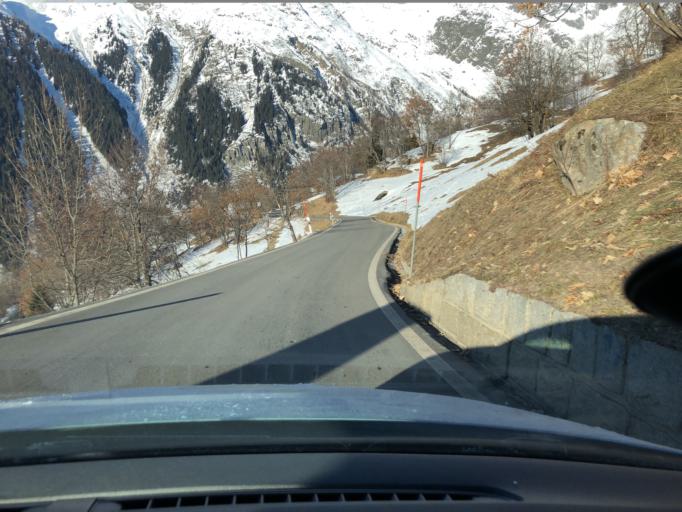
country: CH
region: Valais
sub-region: Goms District
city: Fiesch
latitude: 46.4308
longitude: 8.1524
